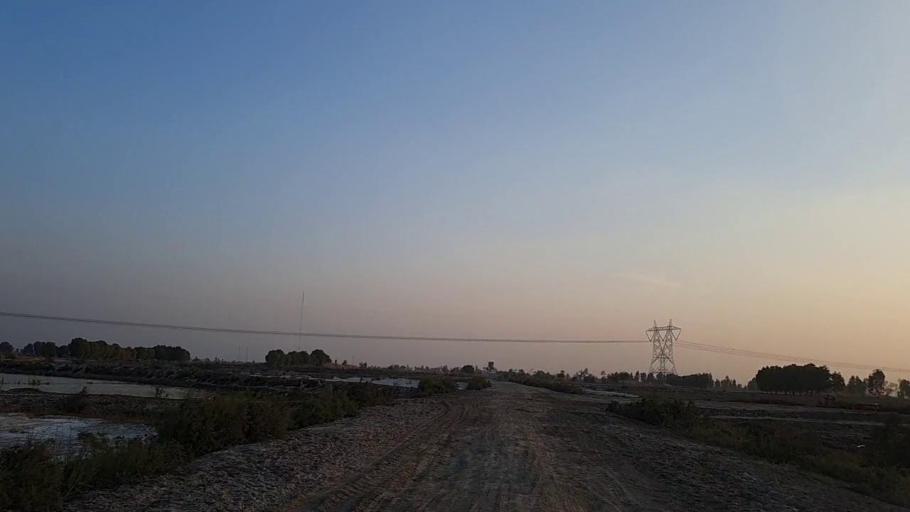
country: PK
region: Sindh
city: Naushahro Firoz
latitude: 26.7788
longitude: 68.0719
